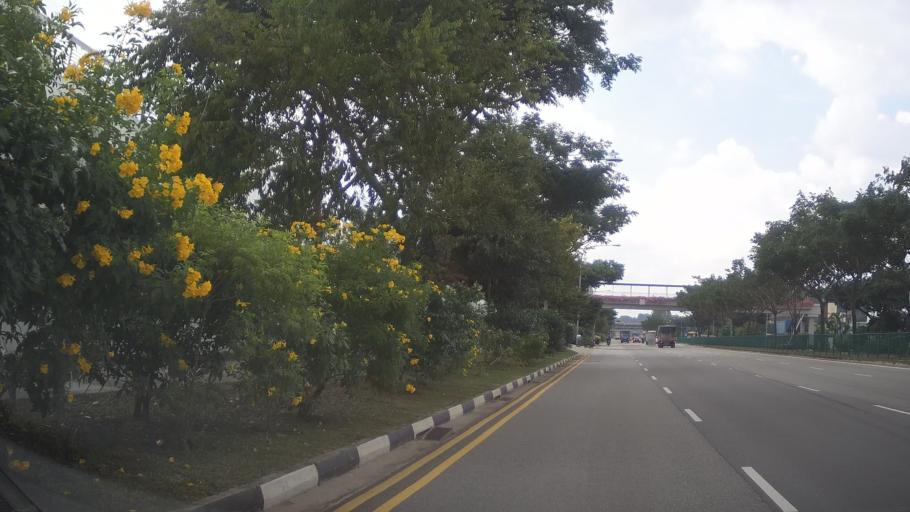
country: MY
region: Johor
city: Johor Bahru
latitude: 1.3175
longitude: 103.6788
